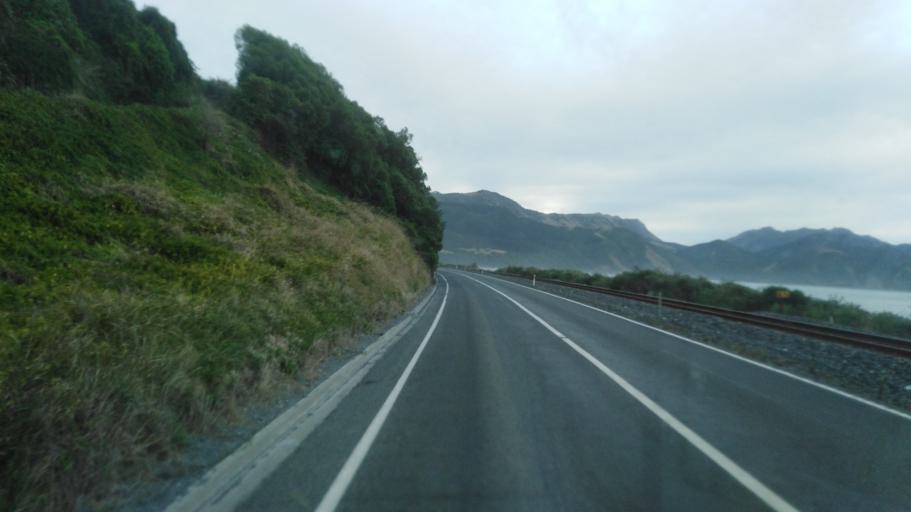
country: NZ
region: Canterbury
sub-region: Kaikoura District
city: Kaikoura
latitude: -42.3098
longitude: 173.7518
